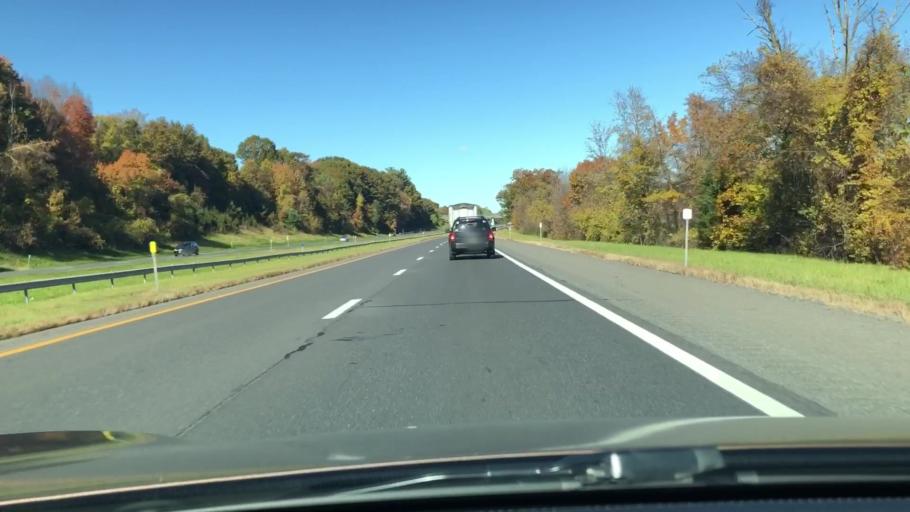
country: US
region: New York
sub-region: Ulster County
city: Lake Katrine
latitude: 41.9949
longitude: -74.0048
